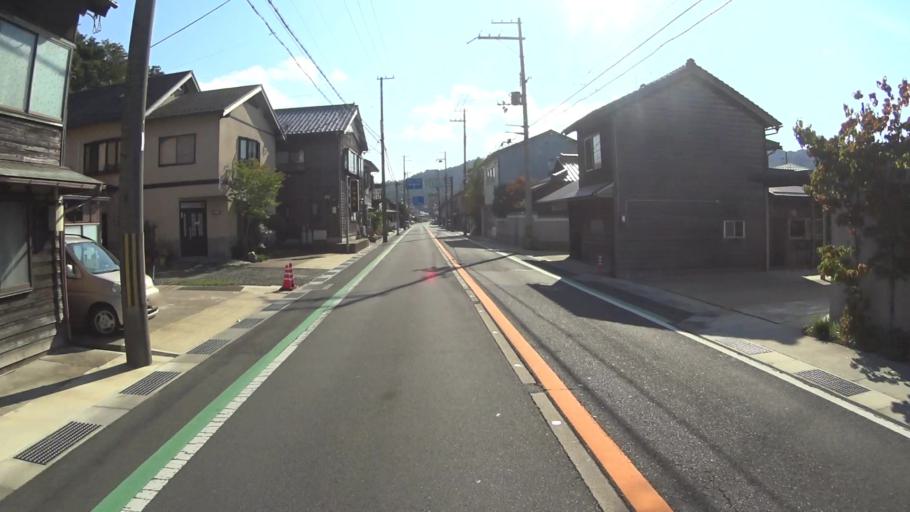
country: JP
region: Kyoto
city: Miyazu
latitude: 35.6791
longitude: 135.0296
